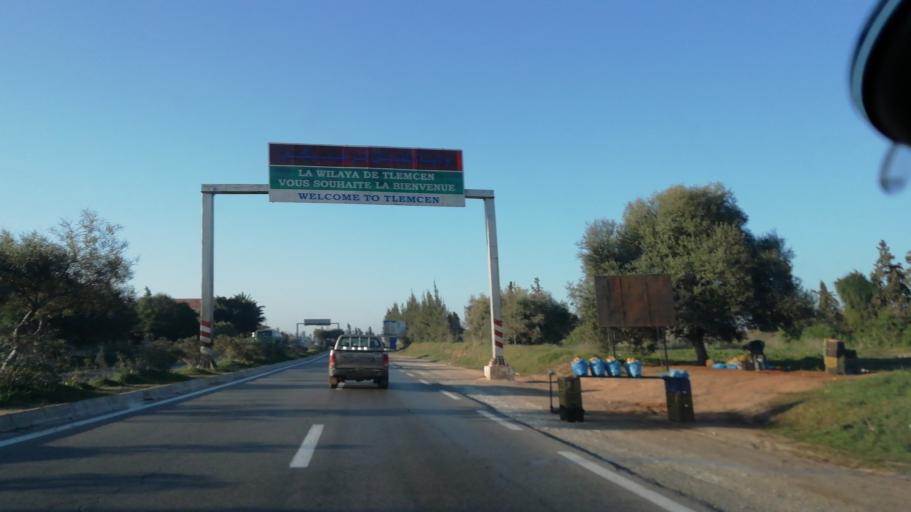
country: DZ
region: Ain Temouchent
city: Beni Saf
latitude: 35.2151
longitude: -1.4142
